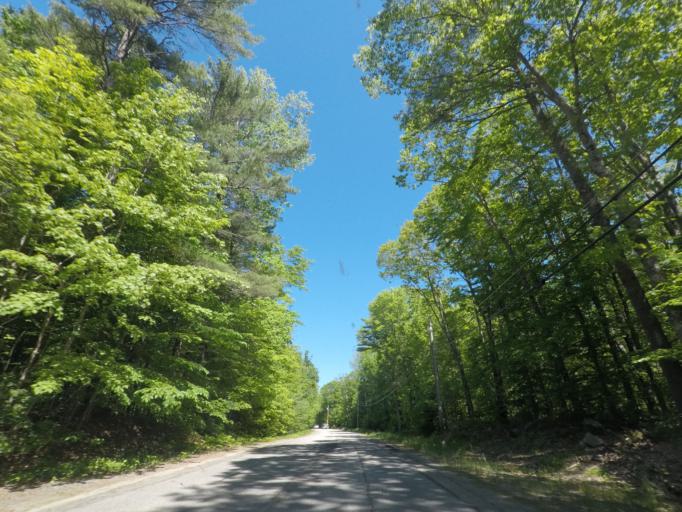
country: US
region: Maine
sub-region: Kennebec County
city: Manchester
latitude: 44.2558
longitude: -69.9026
